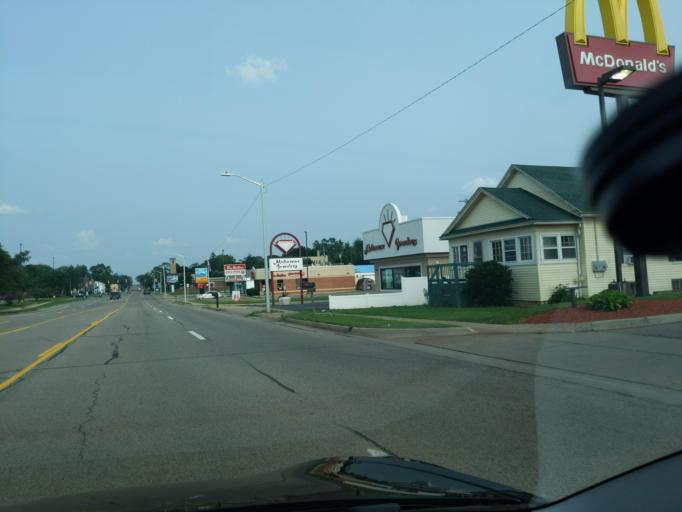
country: US
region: Michigan
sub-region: Jackson County
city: Jackson
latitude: 42.2474
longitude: -84.4365
